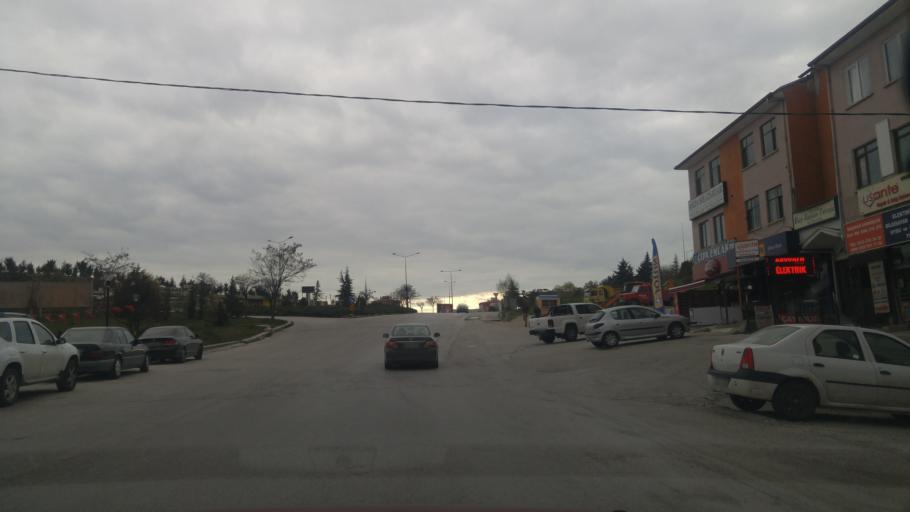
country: TR
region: Ankara
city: Batikent
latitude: 39.8858
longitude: 32.6946
